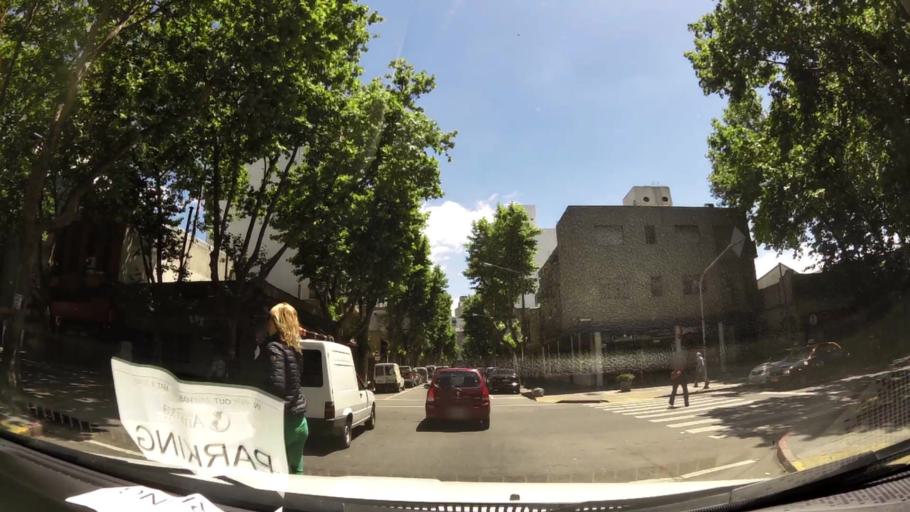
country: UY
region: Montevideo
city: Montevideo
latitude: -34.9023
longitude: -56.1690
